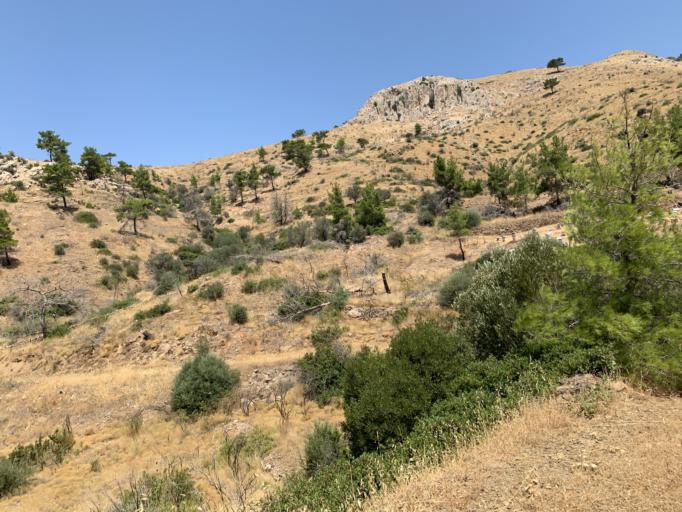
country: GR
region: North Aegean
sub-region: Chios
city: Vrontados
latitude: 38.4370
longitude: 25.9759
